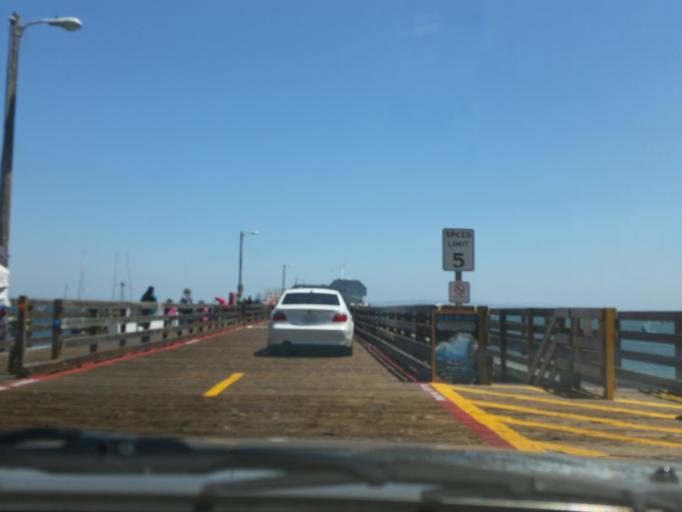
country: US
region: California
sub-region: San Luis Obispo County
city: Avila Beach
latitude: 35.1703
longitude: -120.7554
